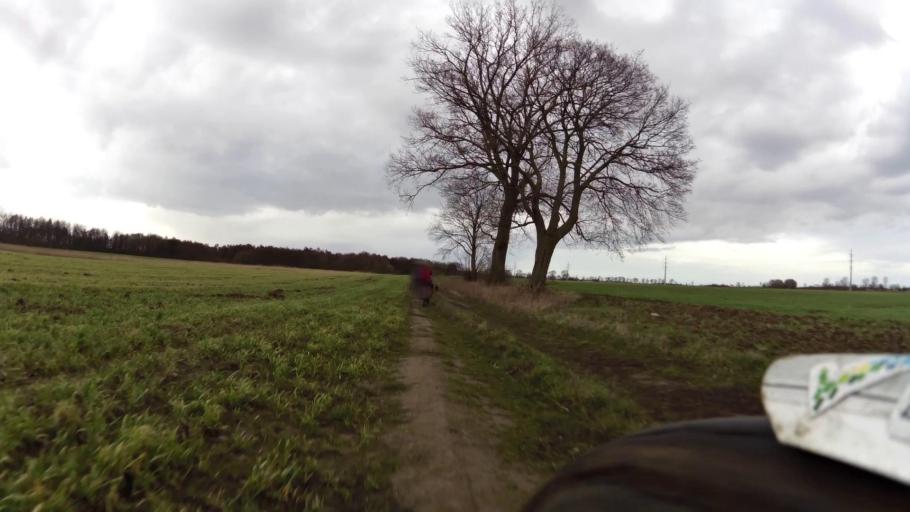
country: PL
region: West Pomeranian Voivodeship
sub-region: Powiat kamienski
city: Kamien Pomorski
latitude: 53.9428
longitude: 14.7677
